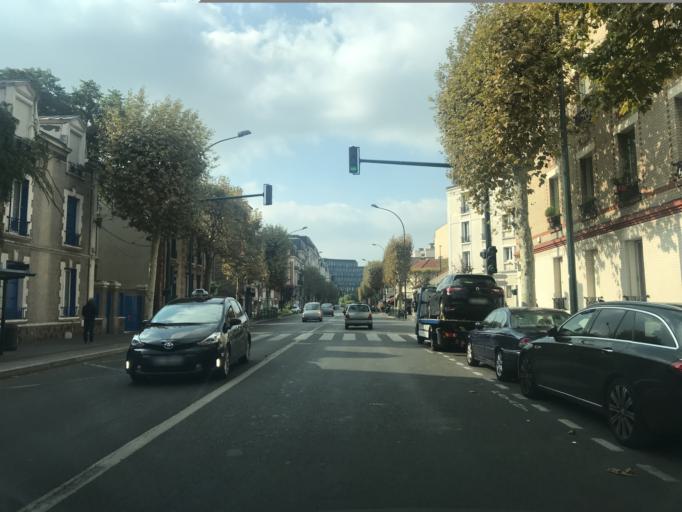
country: FR
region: Ile-de-France
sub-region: Departement des Hauts-de-Seine
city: La Garenne-Colombes
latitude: 48.9068
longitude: 2.2449
